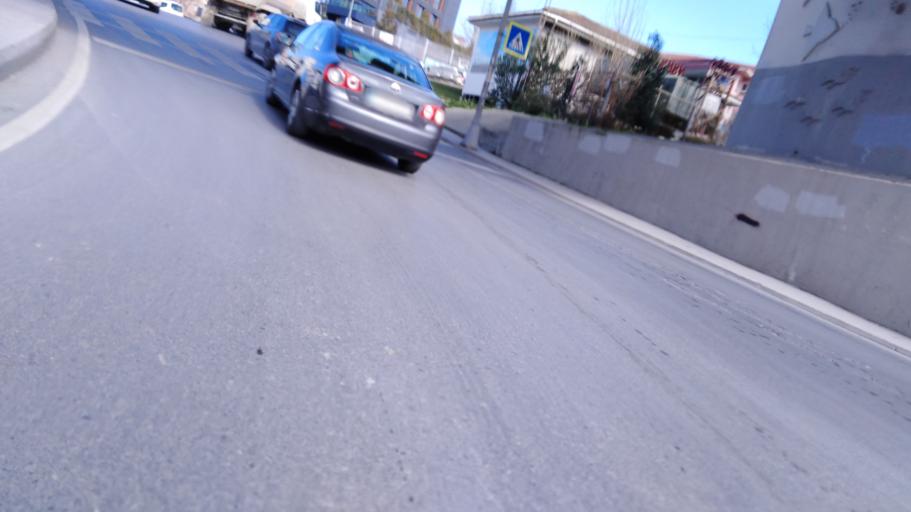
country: TR
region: Istanbul
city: Esenler
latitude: 41.0482
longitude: 28.8986
